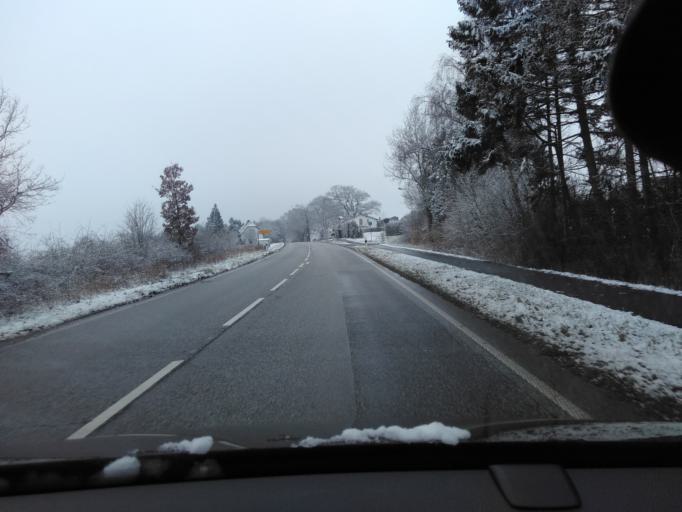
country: DE
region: Schleswig-Holstein
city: Ahrensbok
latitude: 54.0287
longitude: 10.5984
